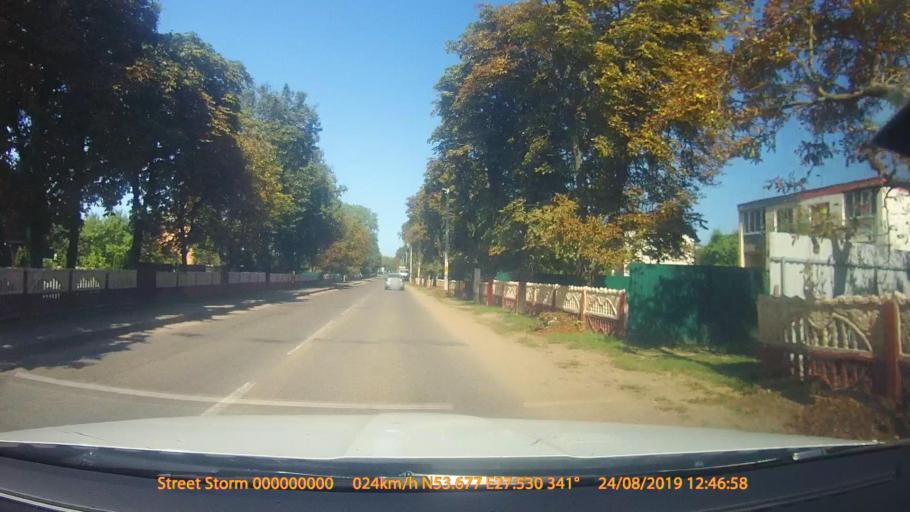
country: BY
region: Minsk
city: Samakhvalavichy
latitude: 53.6772
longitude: 27.5303
